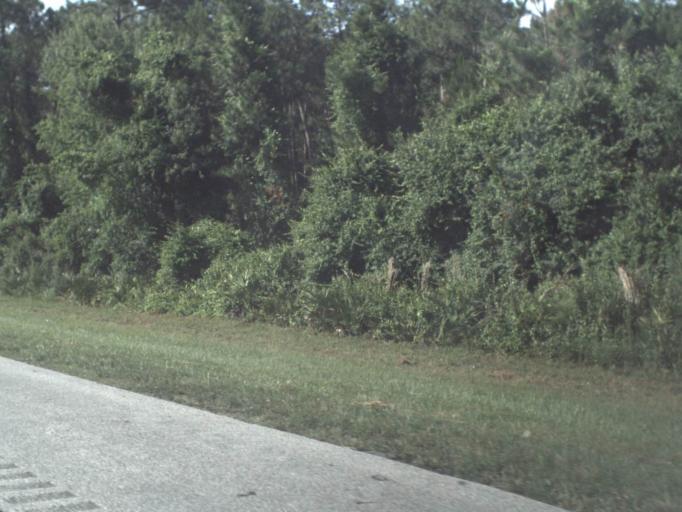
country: US
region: Florida
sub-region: Saint Johns County
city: Saint Augustine Shores
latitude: 29.7948
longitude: -81.3651
